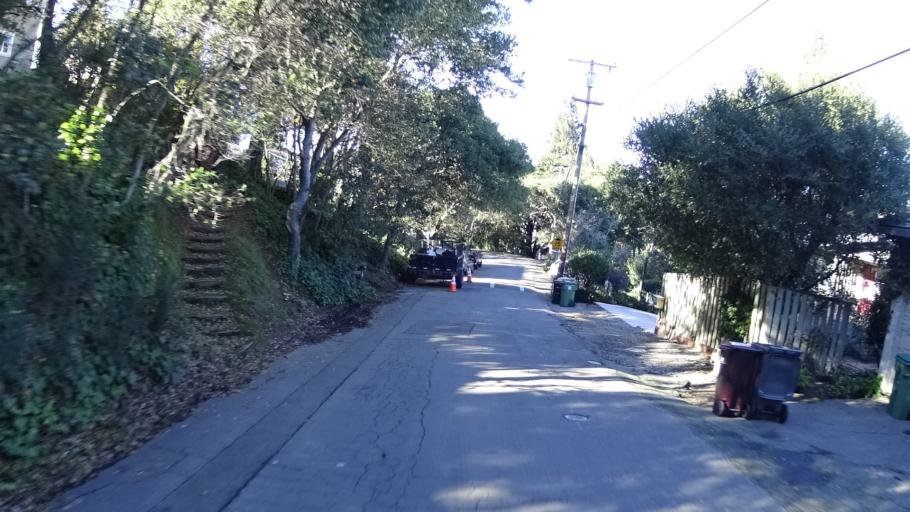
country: US
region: California
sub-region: Alameda County
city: Piedmont
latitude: 37.8362
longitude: -122.2218
